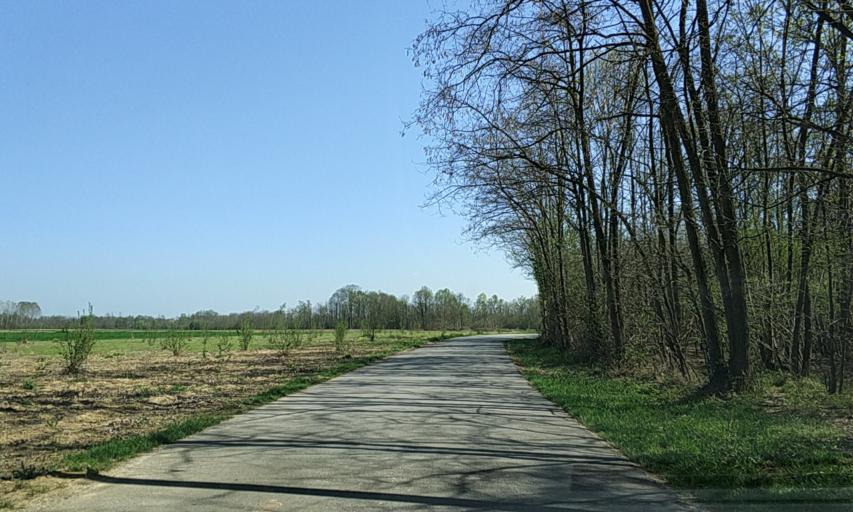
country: IT
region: Piedmont
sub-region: Provincia di Torino
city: Rivara
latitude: 45.3147
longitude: 7.6408
